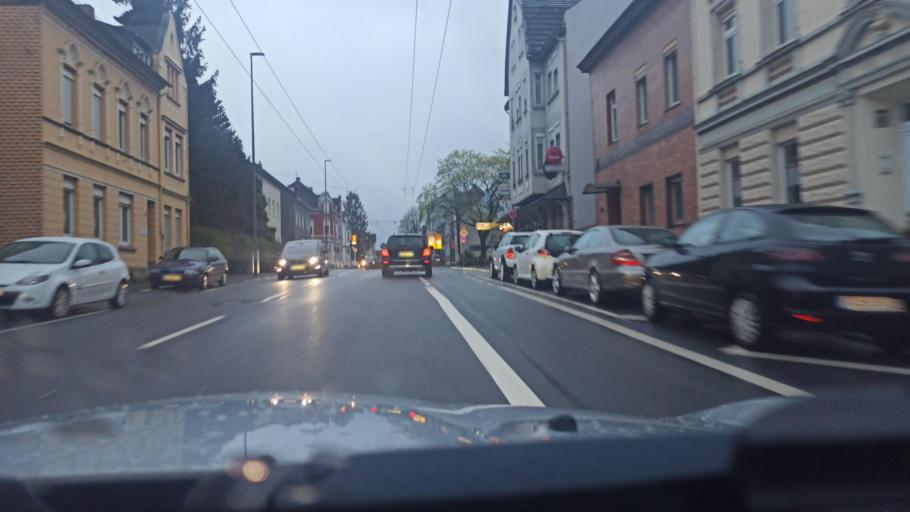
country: DE
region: North Rhine-Westphalia
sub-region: Regierungsbezirk Dusseldorf
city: Solingen
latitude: 51.1950
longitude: 7.0762
